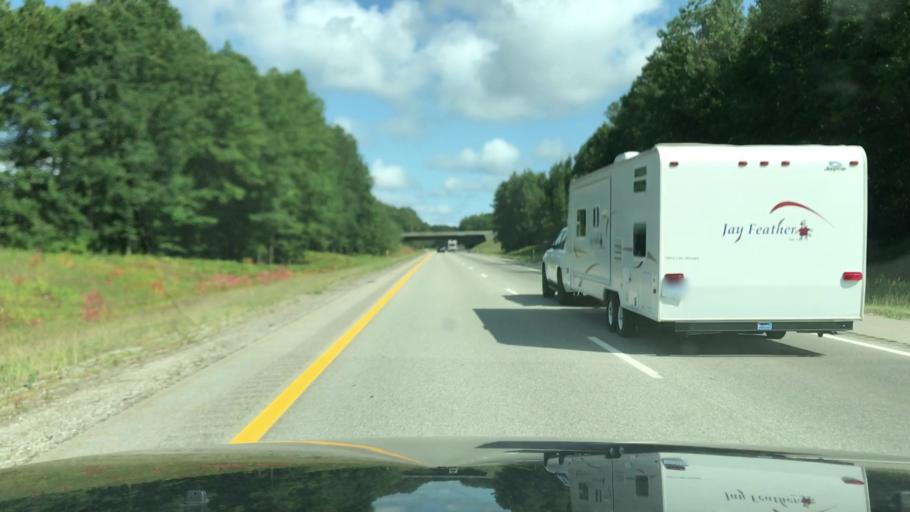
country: US
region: Michigan
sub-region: Montcalm County
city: Howard City
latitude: 43.4864
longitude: -85.4826
